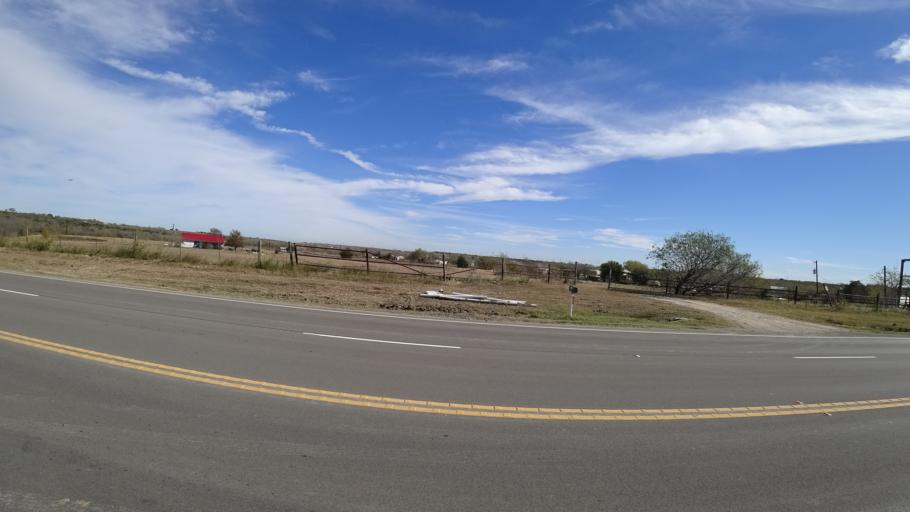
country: US
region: Texas
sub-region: Travis County
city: Onion Creek
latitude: 30.1039
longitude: -97.6945
